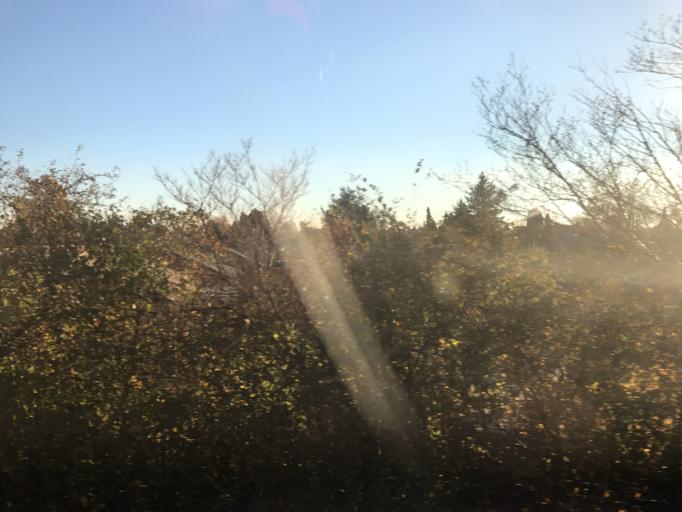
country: DK
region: Capital Region
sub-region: Brondby Kommune
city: Brondbyvester
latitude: 55.6206
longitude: 12.4271
